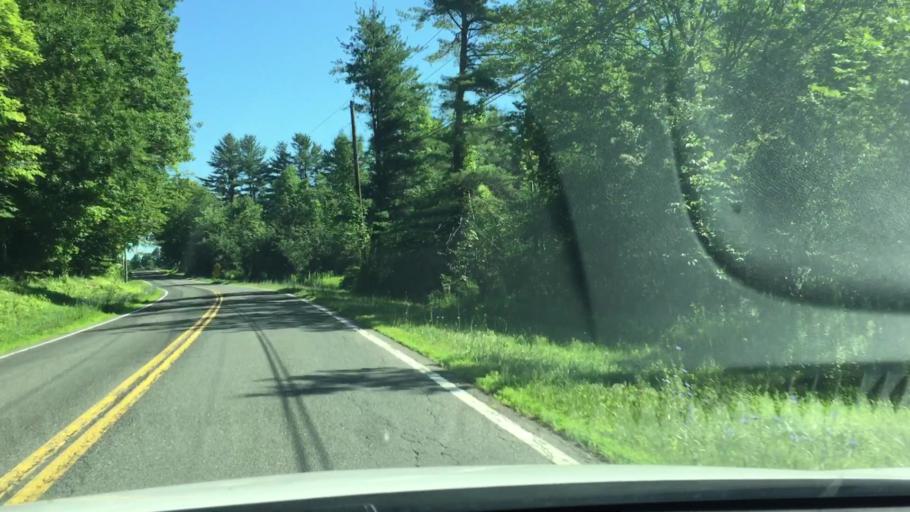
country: US
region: Massachusetts
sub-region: Berkshire County
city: Richmond
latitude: 42.3706
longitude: -73.3470
